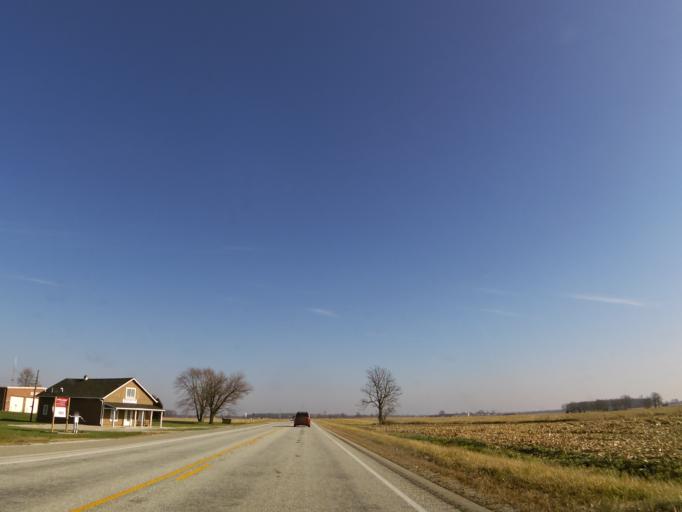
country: US
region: Indiana
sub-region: Shelby County
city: Morristown
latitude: 39.5699
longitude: -85.6186
